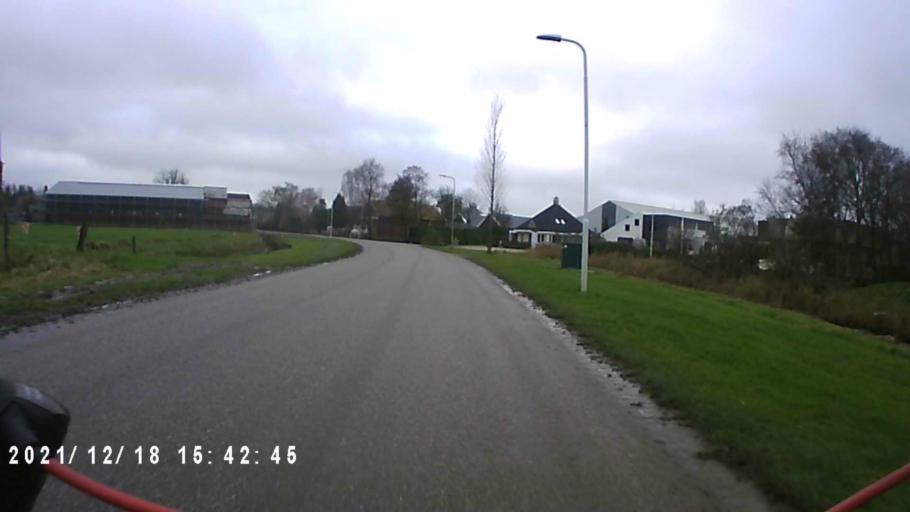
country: NL
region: Friesland
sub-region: Gemeente Dongeradeel
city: Anjum
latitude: 53.3327
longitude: 6.1026
